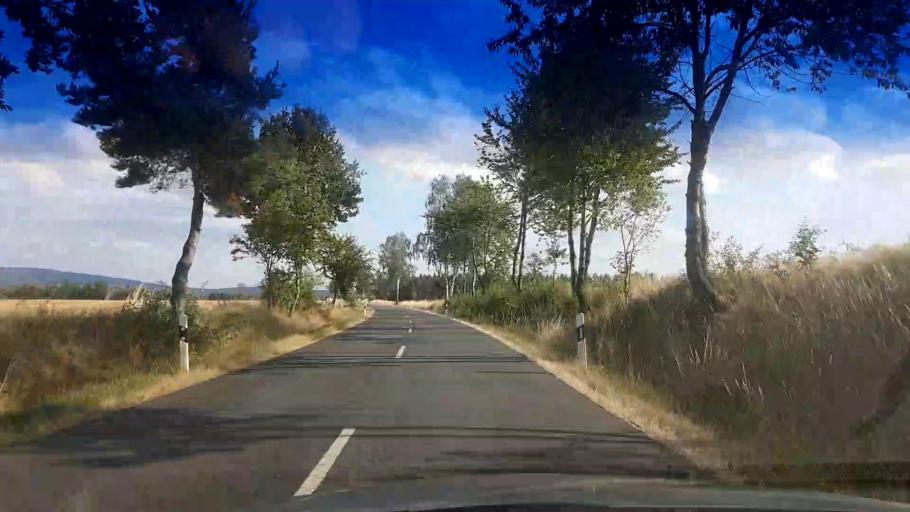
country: DE
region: Bavaria
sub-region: Upper Palatinate
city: Neualbenreuth
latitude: 50.0059
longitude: 12.3810
